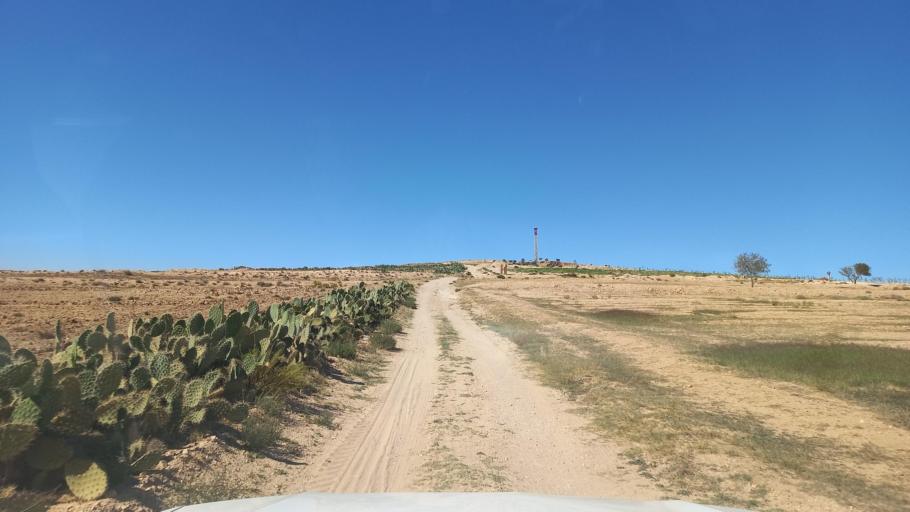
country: TN
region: Al Qasrayn
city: Sbiba
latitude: 35.3737
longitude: 9.0814
